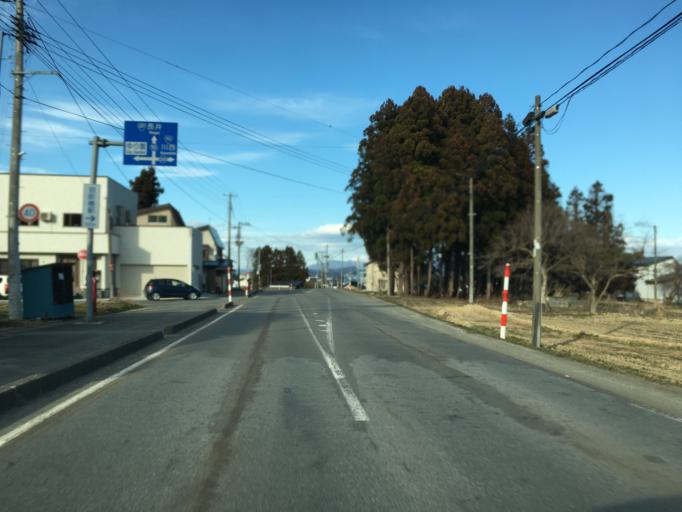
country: JP
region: Yamagata
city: Nagai
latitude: 38.0380
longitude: 139.9893
